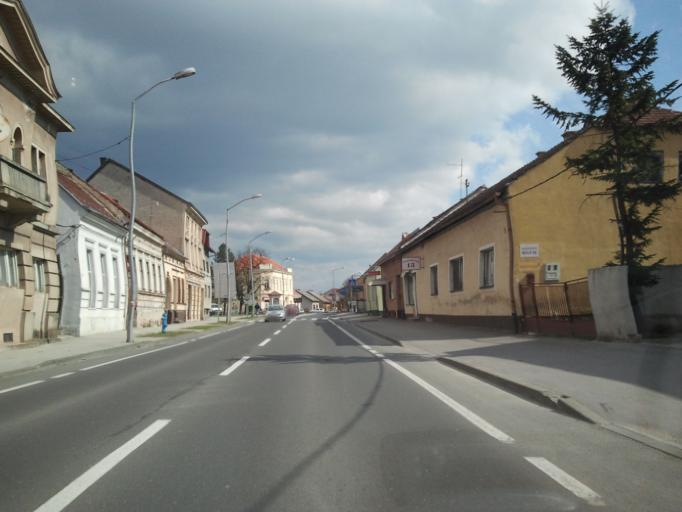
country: HR
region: Zagrebacka
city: Jastrebarsko
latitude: 45.6761
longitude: 15.6550
